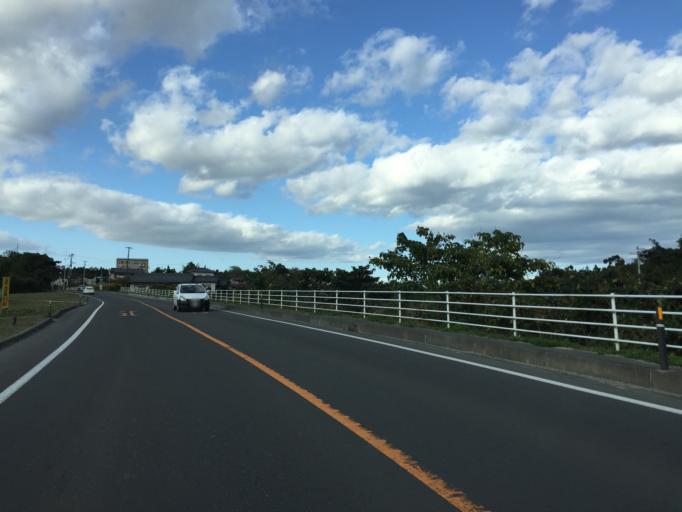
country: JP
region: Miyagi
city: Watari
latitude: 37.9130
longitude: 140.9044
